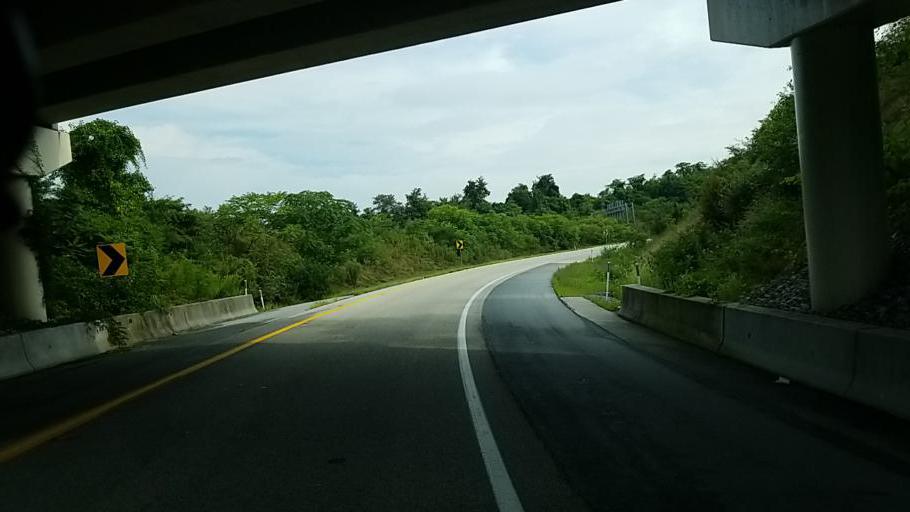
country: US
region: Pennsylvania
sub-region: Perry County
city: Marysville
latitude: 40.3707
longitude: -76.9428
